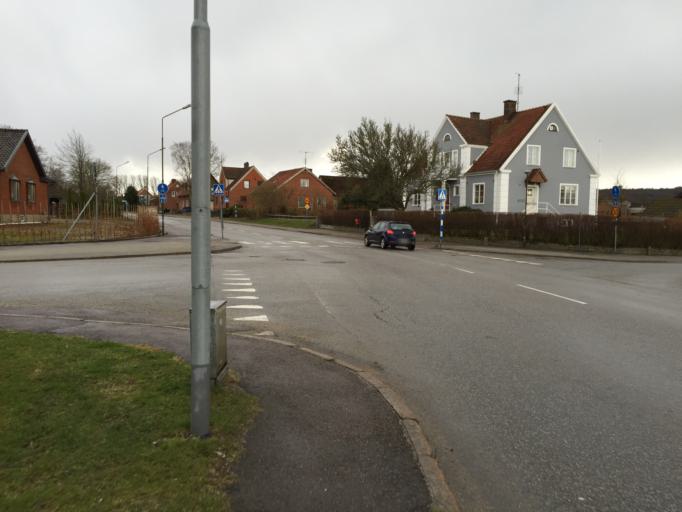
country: SE
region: Skane
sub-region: Lunds Kommun
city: Veberod
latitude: 55.6333
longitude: 13.4922
